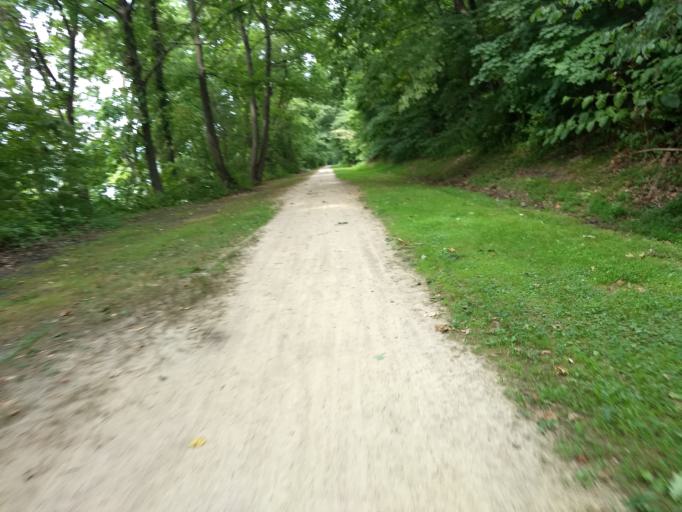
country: US
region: Pennsylvania
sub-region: Allegheny County
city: Brackenridge
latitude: 40.6206
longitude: -79.7044
